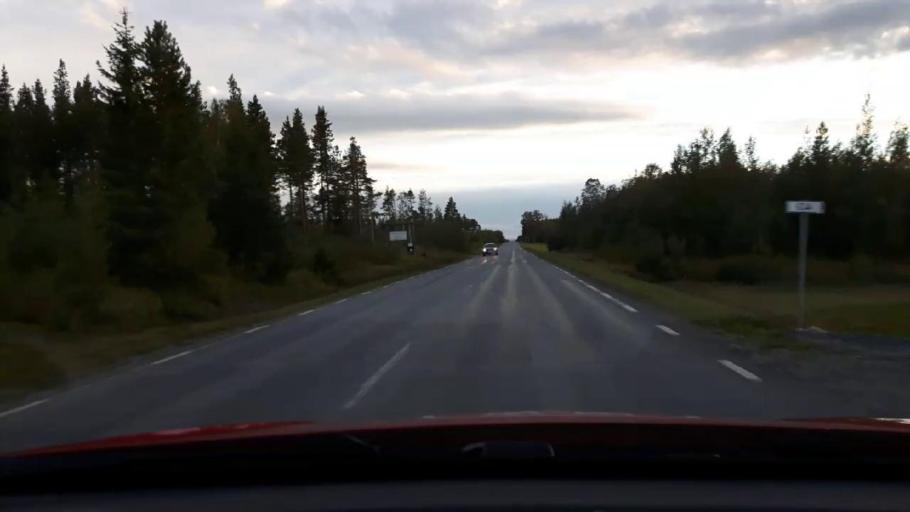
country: SE
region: Jaemtland
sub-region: OEstersunds Kommun
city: Ostersund
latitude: 63.1449
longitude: 14.4757
